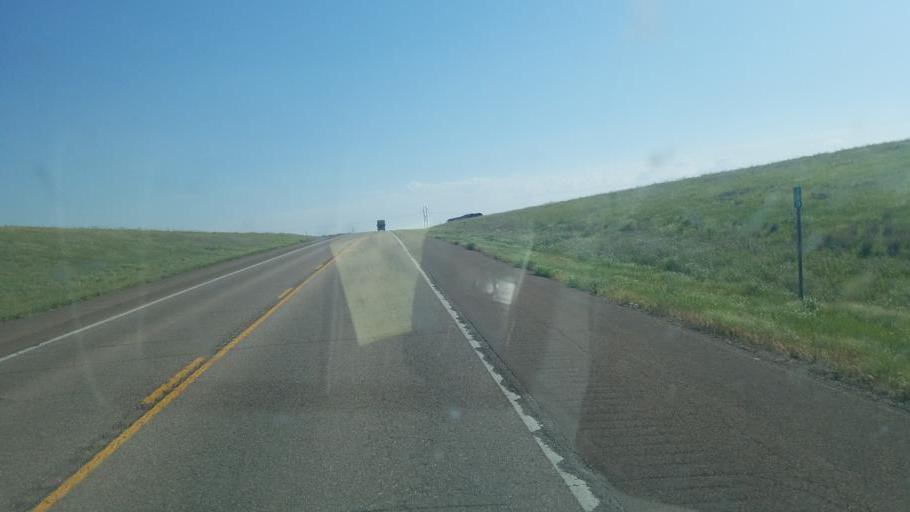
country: US
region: Kansas
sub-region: Barton County
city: Great Bend
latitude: 38.3851
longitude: -98.6808
